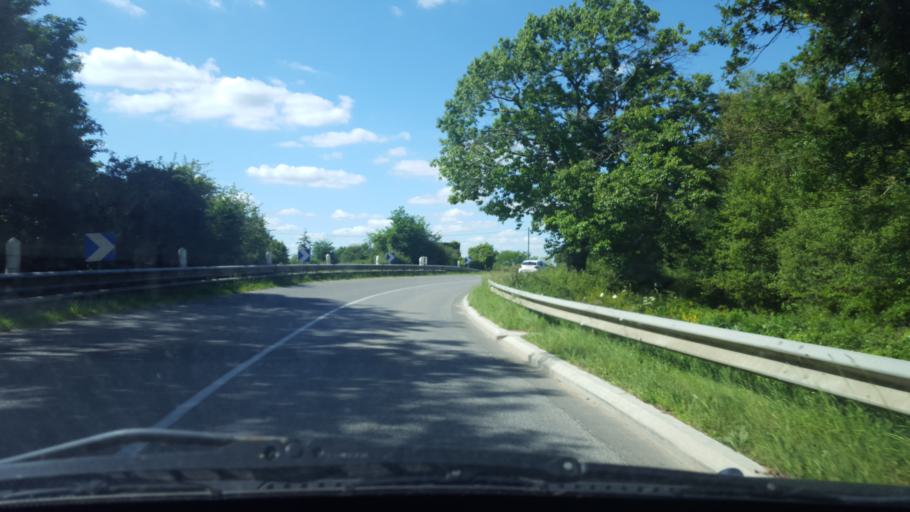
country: FR
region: Pays de la Loire
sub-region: Departement de la Loire-Atlantique
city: La Chevroliere
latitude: 47.0575
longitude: -1.5705
